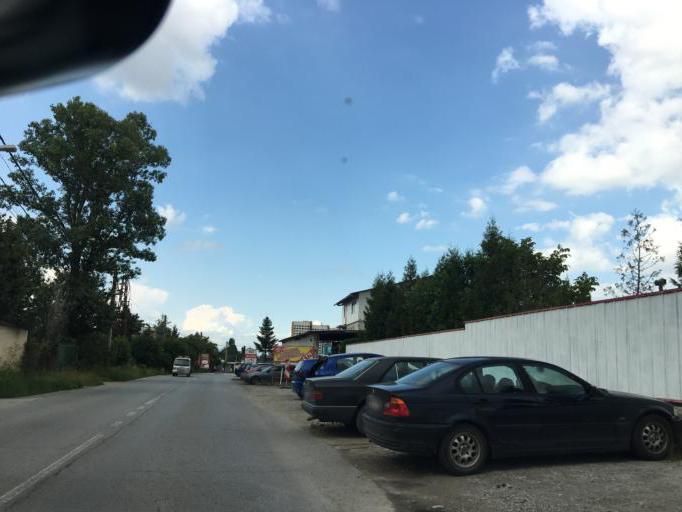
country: BG
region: Sofia-Capital
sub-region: Stolichna Obshtina
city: Sofia
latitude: 42.6414
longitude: 23.3530
